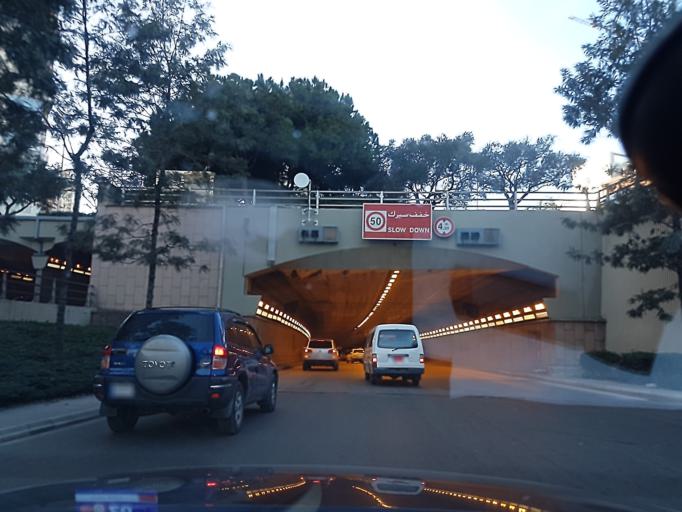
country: LB
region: Beyrouth
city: Beirut
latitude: 33.8941
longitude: 35.5001
